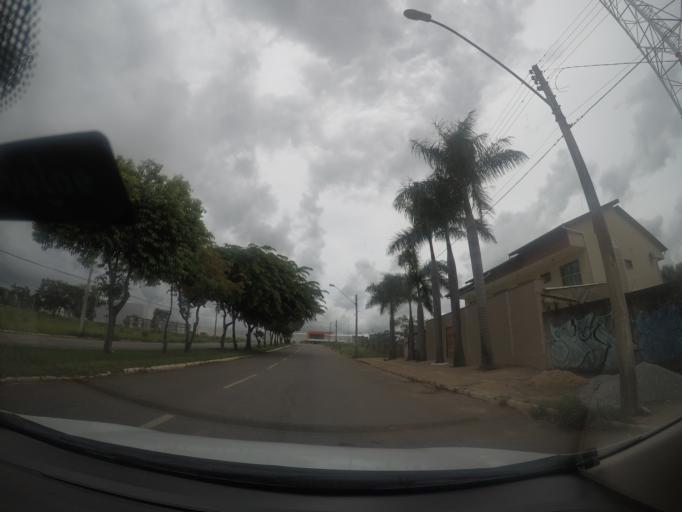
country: BR
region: Goias
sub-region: Trindade
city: Trindade
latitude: -16.6570
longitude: -49.3850
